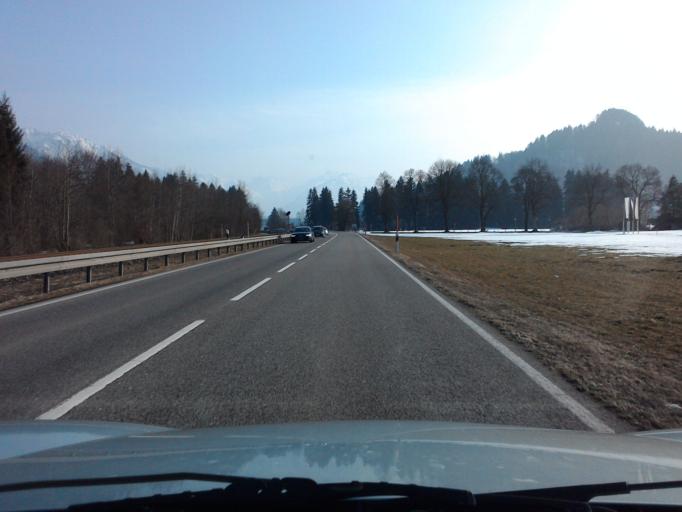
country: DE
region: Bavaria
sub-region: Swabia
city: Obermaiselstein
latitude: 47.4490
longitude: 10.2726
